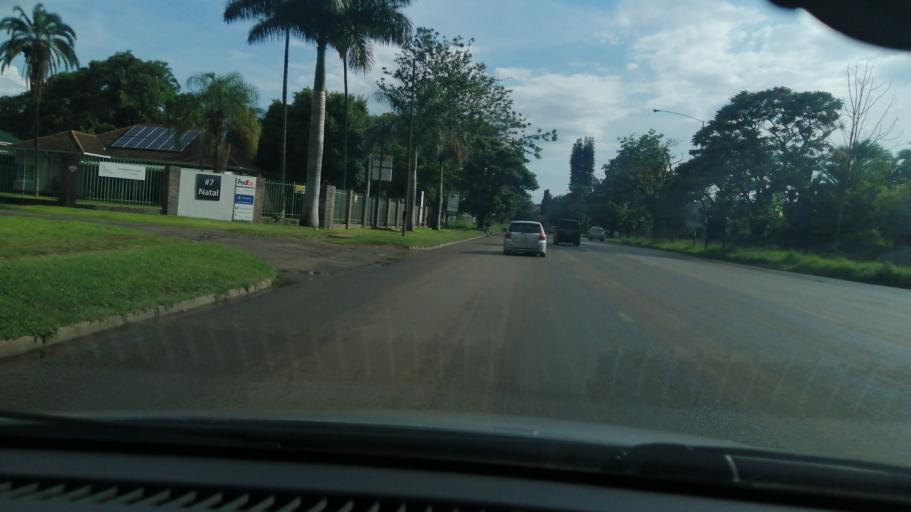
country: ZW
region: Harare
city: Harare
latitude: -17.7993
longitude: 31.0450
